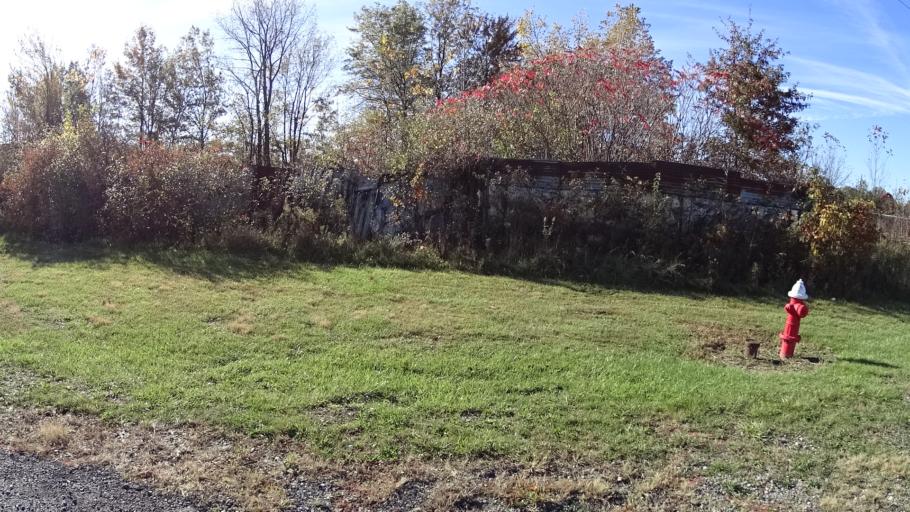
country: US
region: Ohio
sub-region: Lorain County
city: Lorain
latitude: 41.4373
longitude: -82.1621
